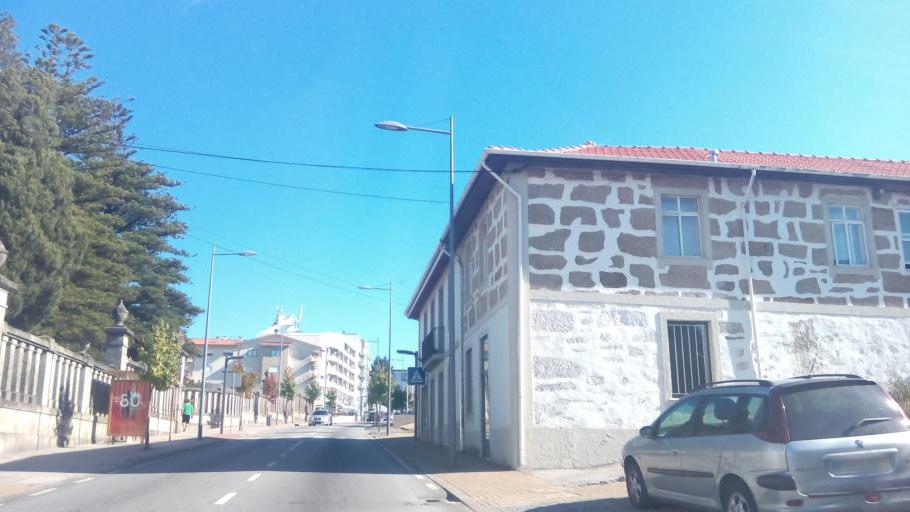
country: PT
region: Porto
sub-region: Penafiel
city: Penafiel
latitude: 41.1958
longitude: -8.2953
